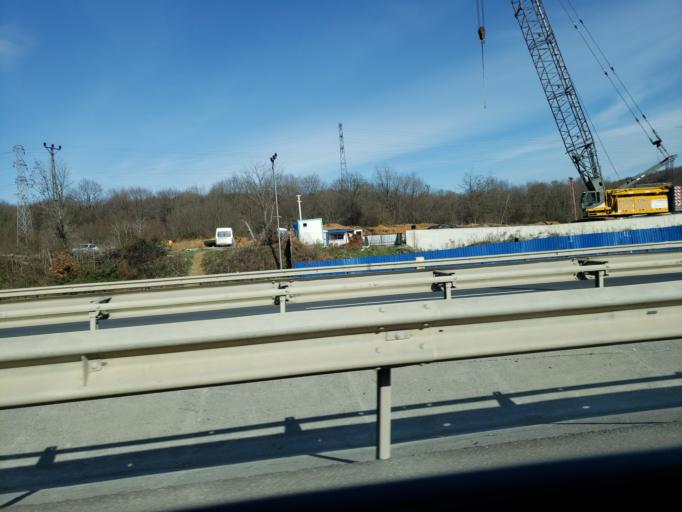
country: TR
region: Istanbul
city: Kemerburgaz
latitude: 41.2010
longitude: 28.8604
